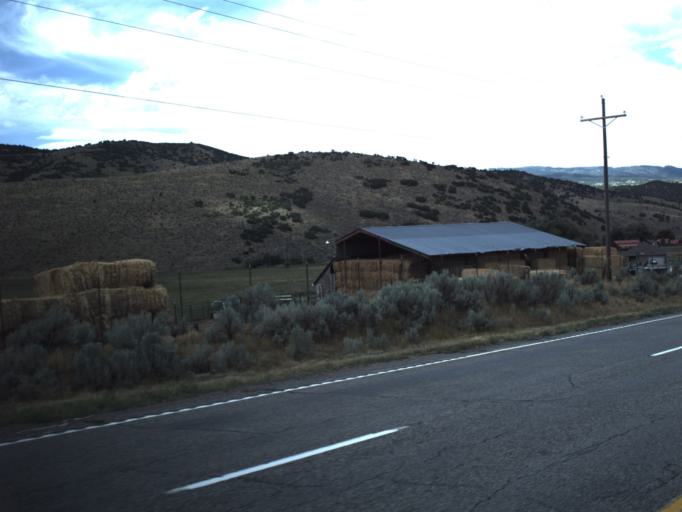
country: US
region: Utah
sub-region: Utah County
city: Woodland Hills
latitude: 39.8583
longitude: -111.5252
